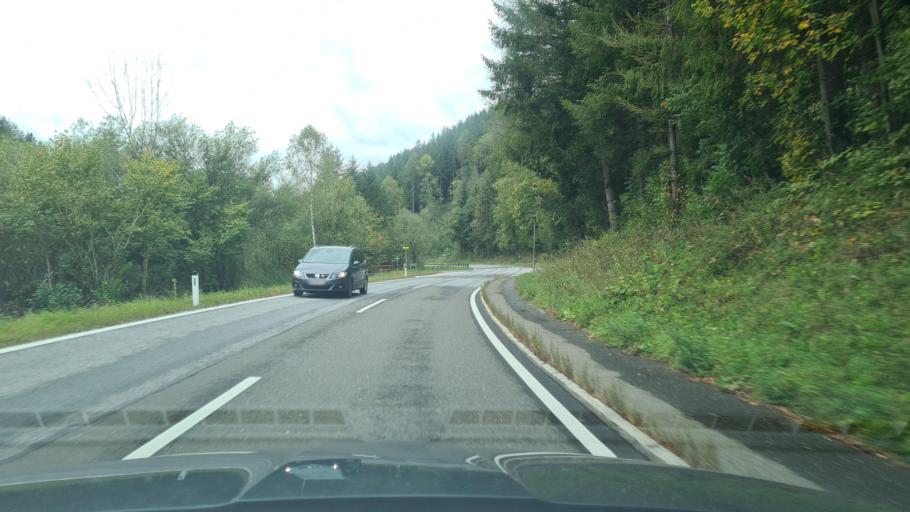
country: AT
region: Styria
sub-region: Politischer Bezirk Weiz
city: Gasen
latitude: 47.3842
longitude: 15.4747
